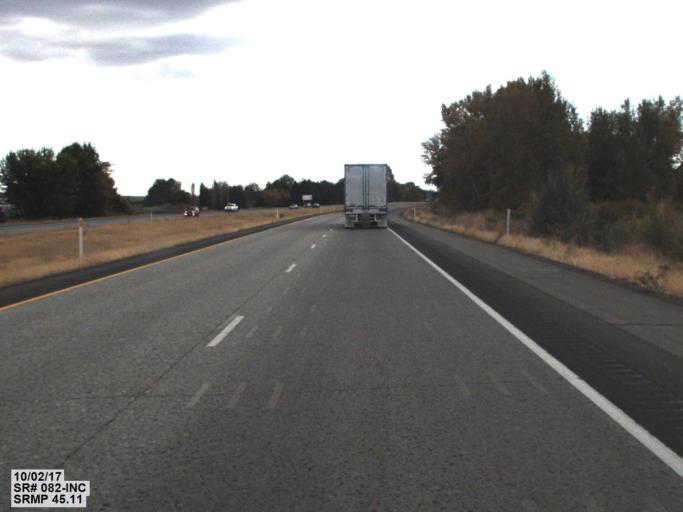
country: US
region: Washington
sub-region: Yakima County
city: Wapato
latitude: 46.4651
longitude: -120.3826
